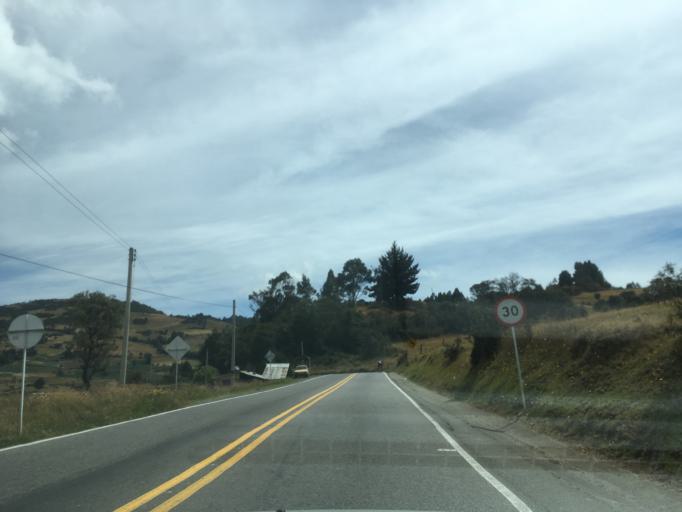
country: CO
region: Boyaca
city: Firavitoba
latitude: 5.6219
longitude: -72.9109
